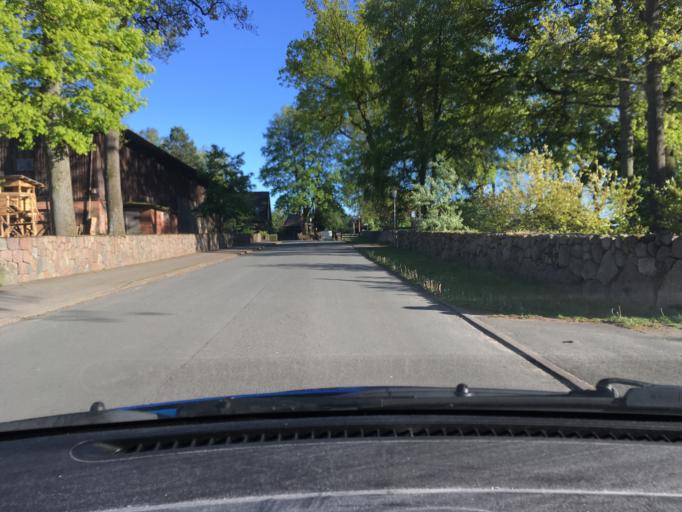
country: DE
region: Lower Saxony
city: Soderstorf
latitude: 53.1274
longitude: 10.1685
